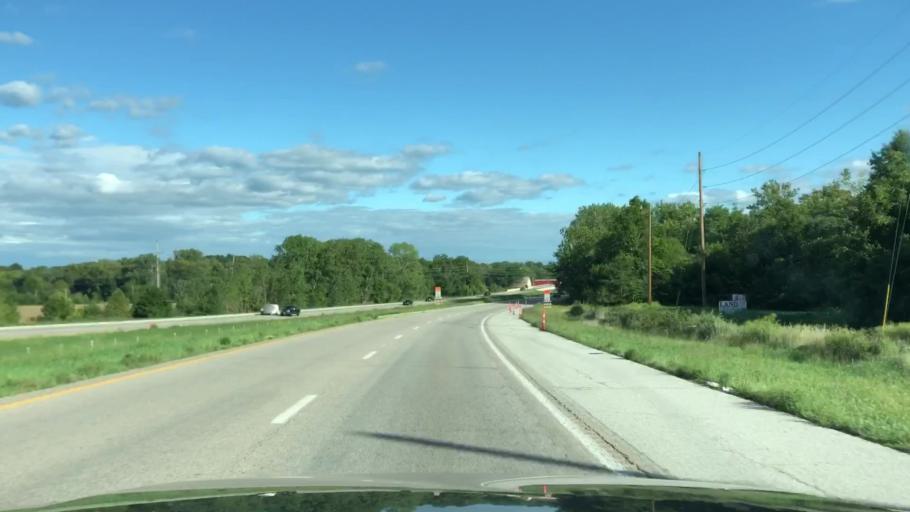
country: US
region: Missouri
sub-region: Saint Charles County
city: Wentzville
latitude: 38.8610
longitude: -90.8775
